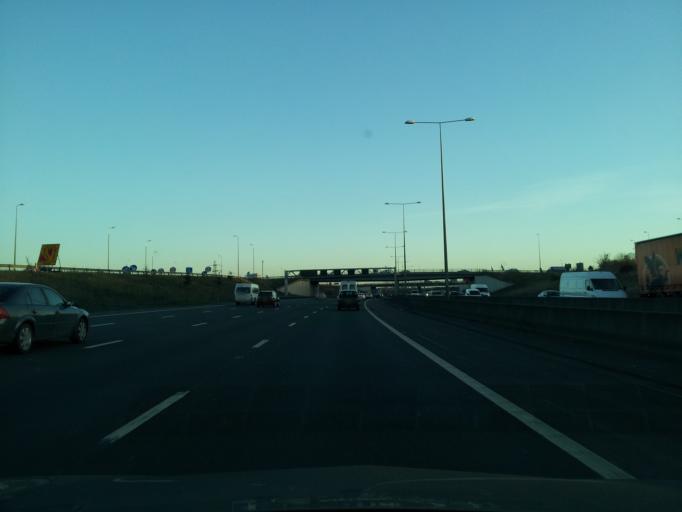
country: GB
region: England
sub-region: Luton
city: Luton
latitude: 51.8562
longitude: -0.4253
